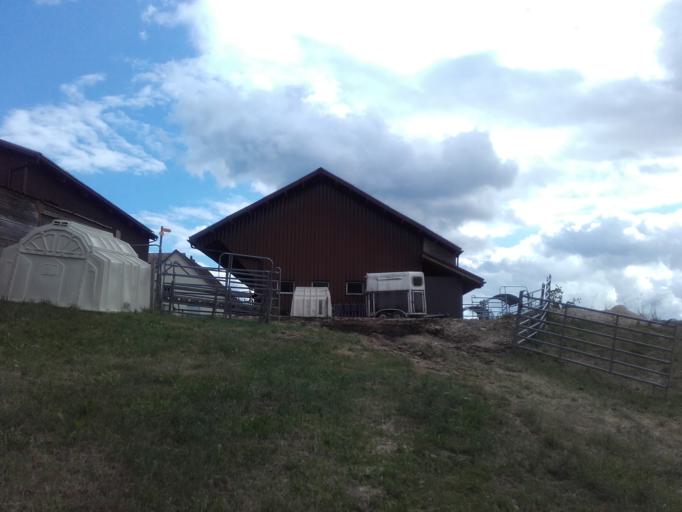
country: CH
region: Solothurn
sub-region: Bezirk Thal
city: Matzendorf
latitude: 47.3166
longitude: 7.6006
